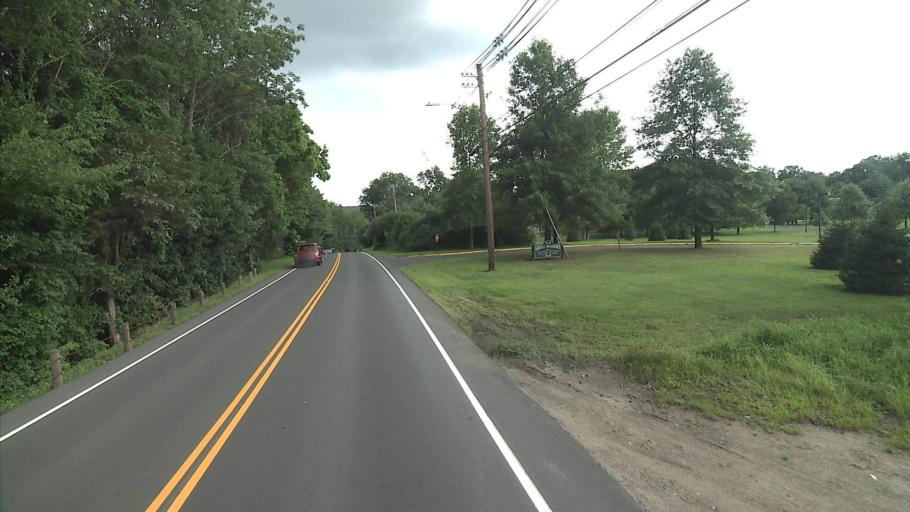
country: US
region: Connecticut
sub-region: New Haven County
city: Heritage Village
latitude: 41.5017
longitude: -73.2236
